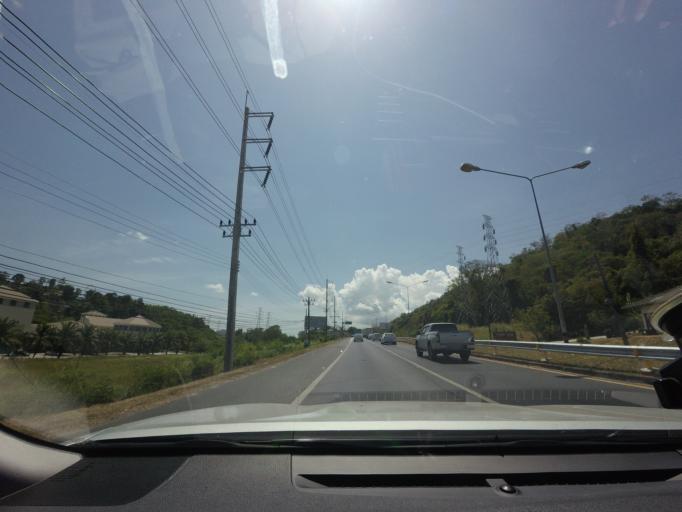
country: TH
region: Phuket
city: Ban Ko Kaeo
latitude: 7.9453
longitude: 98.3835
